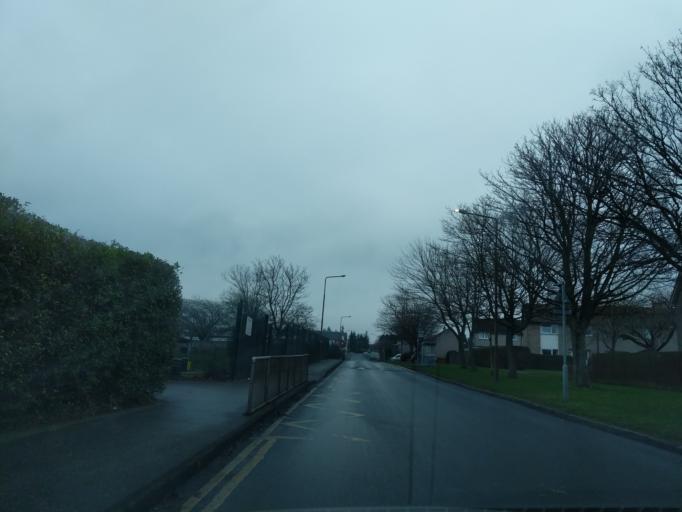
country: GB
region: Scotland
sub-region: Edinburgh
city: Currie
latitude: 55.8982
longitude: -3.3142
